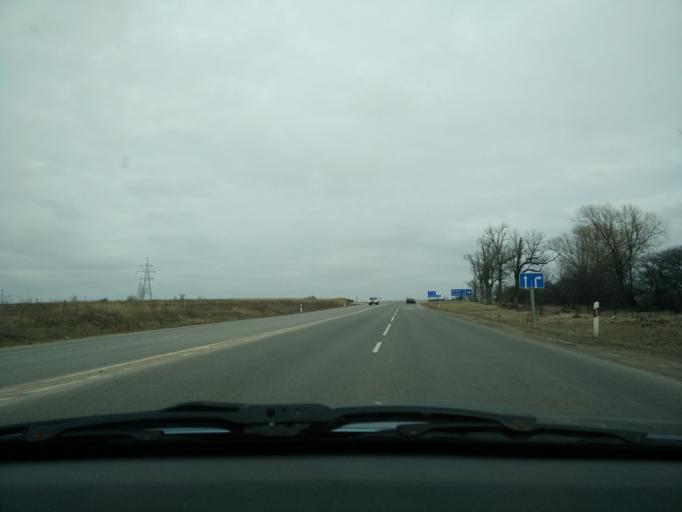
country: LT
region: Klaipedos apskritis
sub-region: Klaipeda
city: Klaipeda
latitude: 55.7292
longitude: 21.1789
